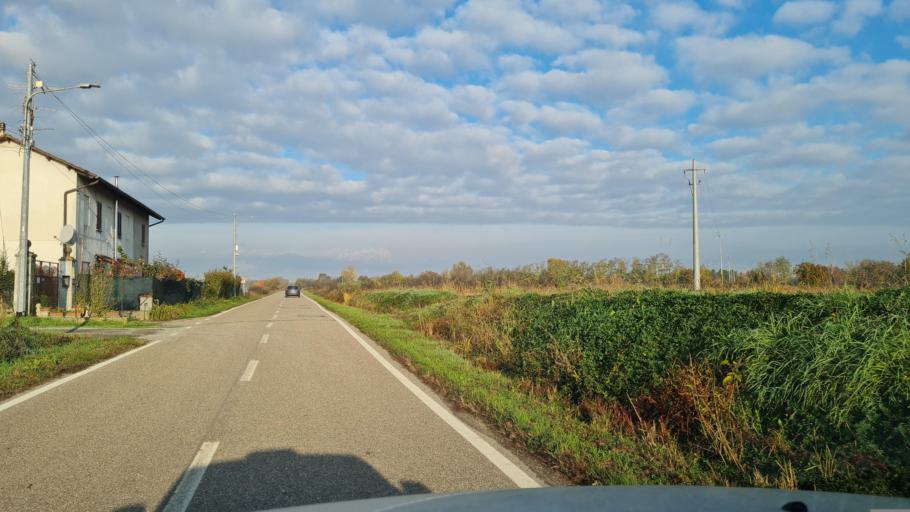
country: IT
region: Piedmont
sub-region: Provincia di Vercelli
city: Villarboit
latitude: 45.4403
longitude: 8.3347
